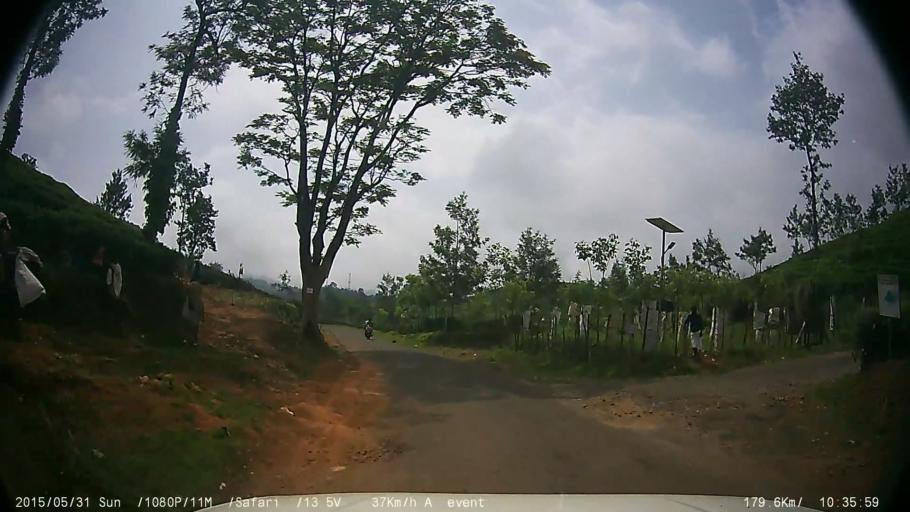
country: IN
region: Kerala
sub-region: Wayanad
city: Kalpetta
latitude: 11.5041
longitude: 76.1459
